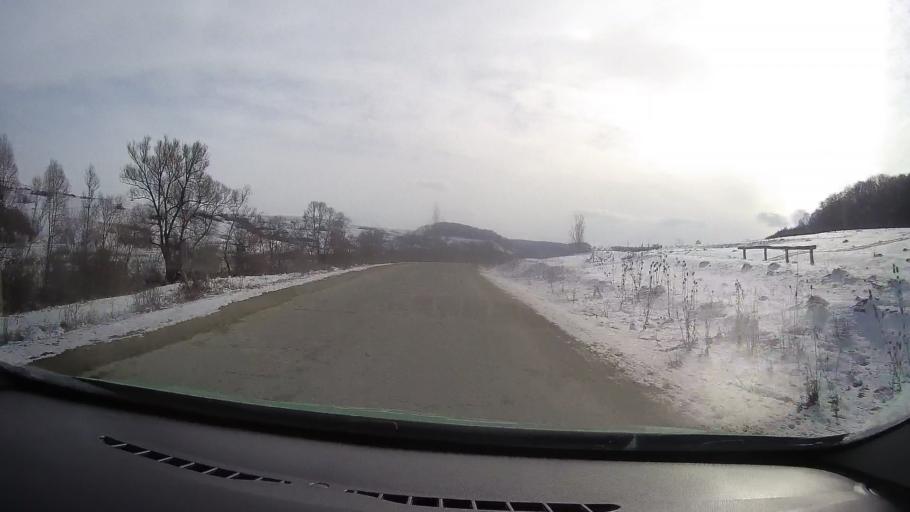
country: RO
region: Sibiu
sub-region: Comuna Bradeni
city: Bradeni
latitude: 46.0917
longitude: 24.8339
